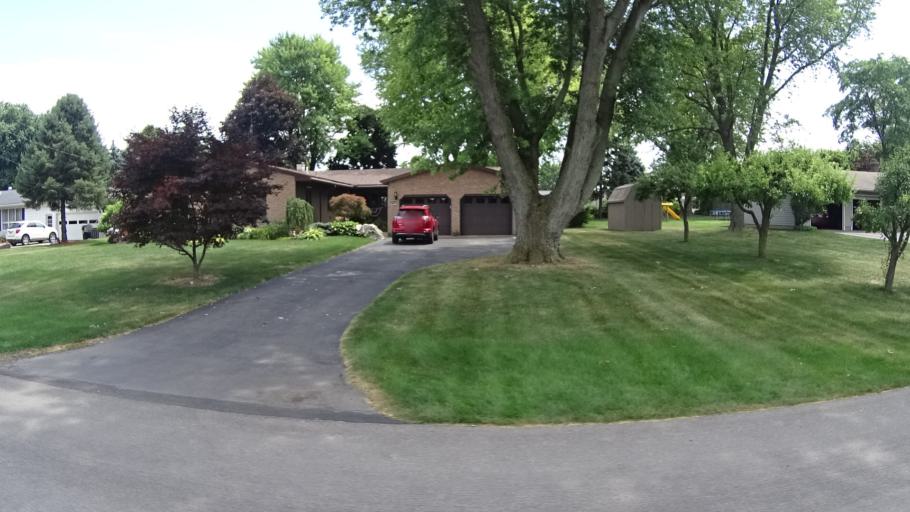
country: US
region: Ohio
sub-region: Erie County
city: Sandusky
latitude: 41.3971
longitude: -82.7837
